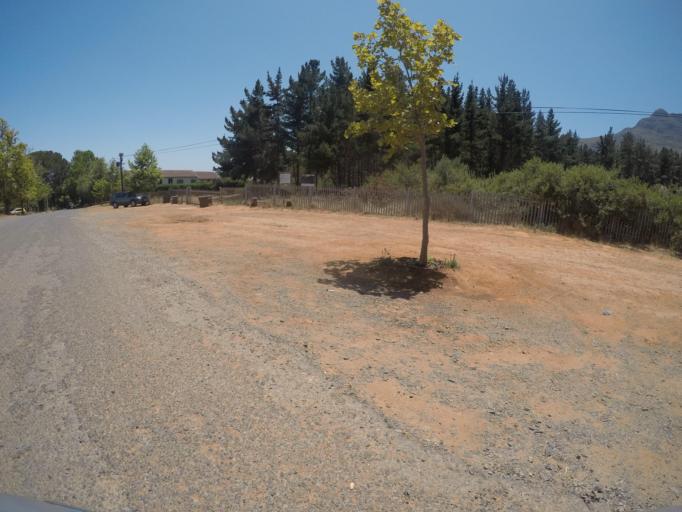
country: ZA
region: Western Cape
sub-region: Cape Winelands District Municipality
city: Stellenbosch
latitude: -33.9691
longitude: 18.8653
